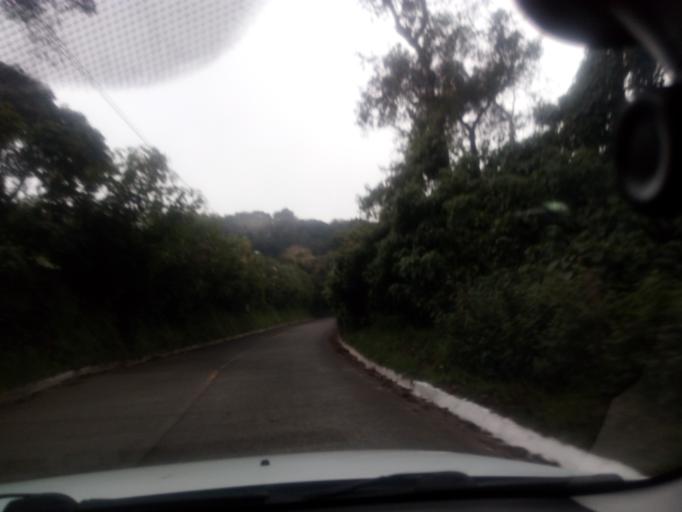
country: GT
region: Sacatepequez
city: San Bartolome Milpas Altas
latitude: 14.5964
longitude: -90.6848
